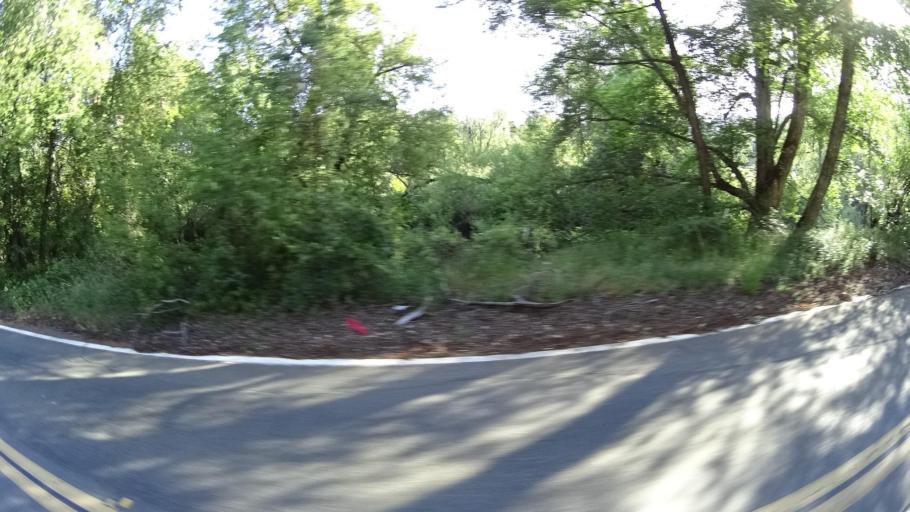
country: US
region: California
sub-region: Lake County
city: North Lakeport
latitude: 39.1116
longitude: -122.9786
